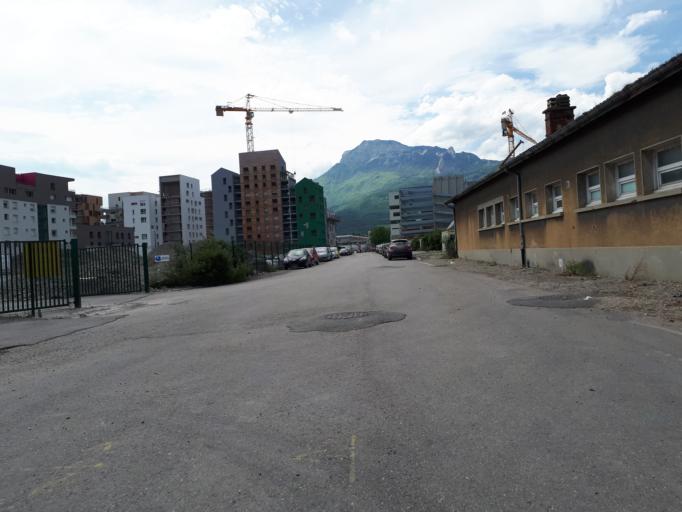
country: FR
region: Rhone-Alpes
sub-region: Departement de l'Isere
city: Saint-Martin-le-Vinoux
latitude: 45.2042
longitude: 5.7062
